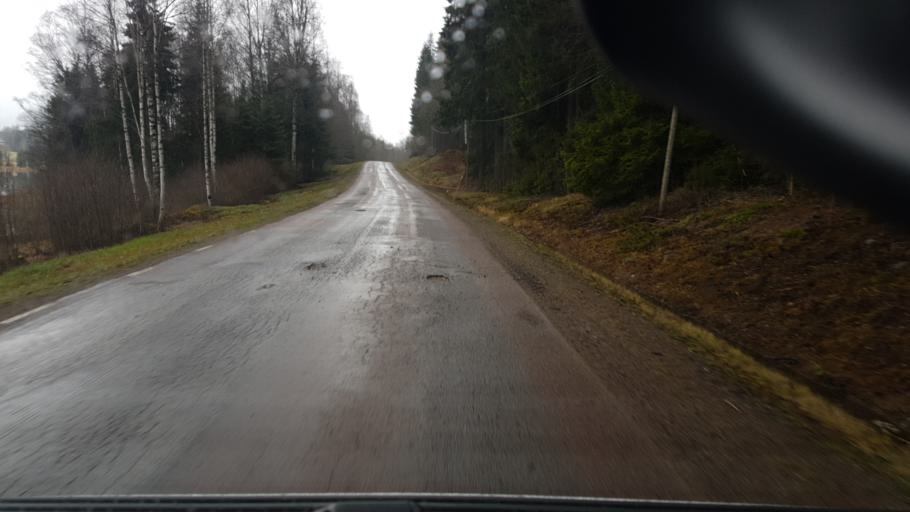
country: SE
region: Vaermland
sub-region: Eda Kommun
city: Amotfors
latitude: 59.9005
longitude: 12.5255
